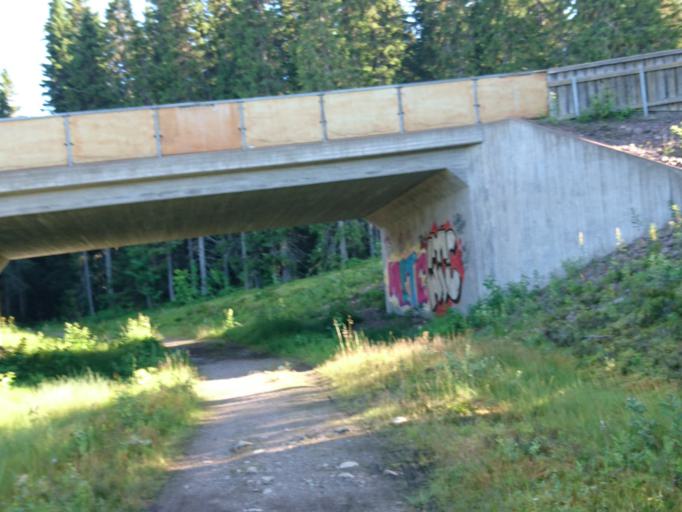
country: SE
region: Dalarna
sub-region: Malung-Saelens kommun
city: Malung
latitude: 61.1698
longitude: 13.1772
